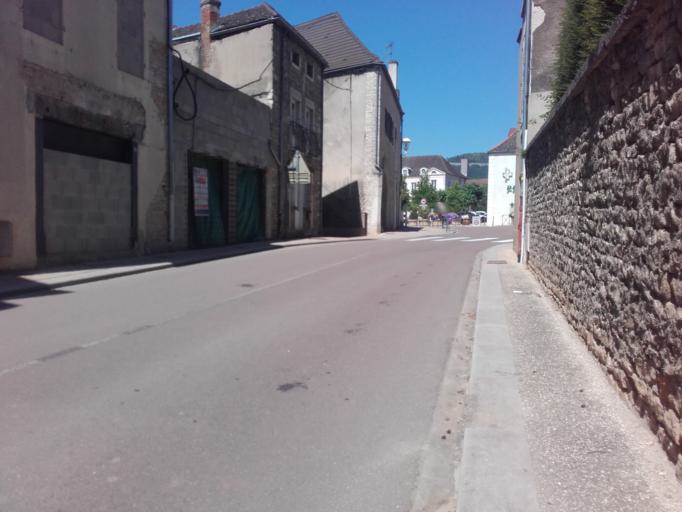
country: FR
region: Bourgogne
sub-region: Departement de Saone-et-Loire
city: Chagny
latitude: 46.9112
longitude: 4.7011
